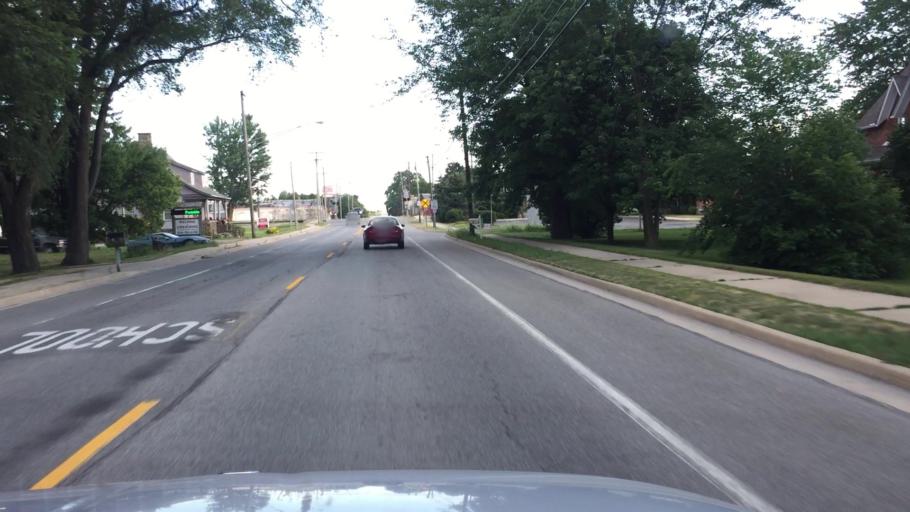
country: US
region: Michigan
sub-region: Macomb County
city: Memphis
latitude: 42.9921
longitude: -82.7653
